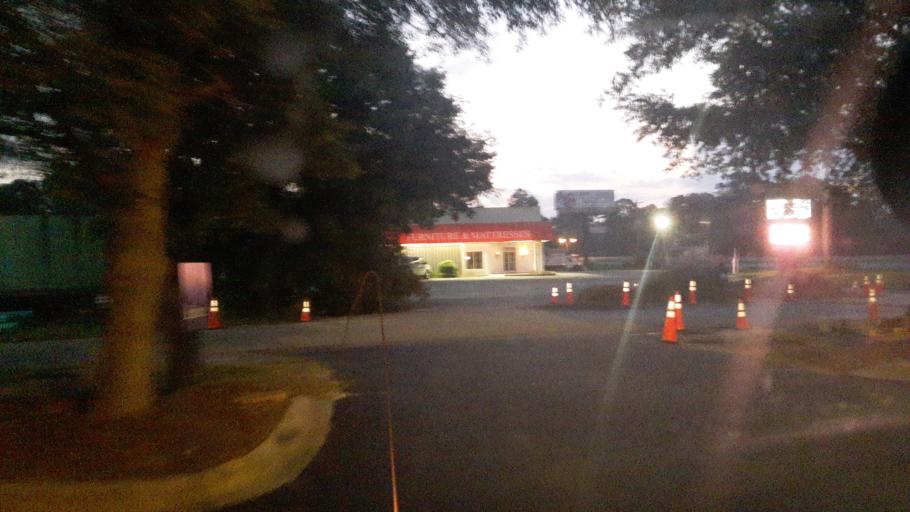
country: US
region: South Carolina
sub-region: Horry County
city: Little River
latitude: 33.8688
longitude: -78.6317
